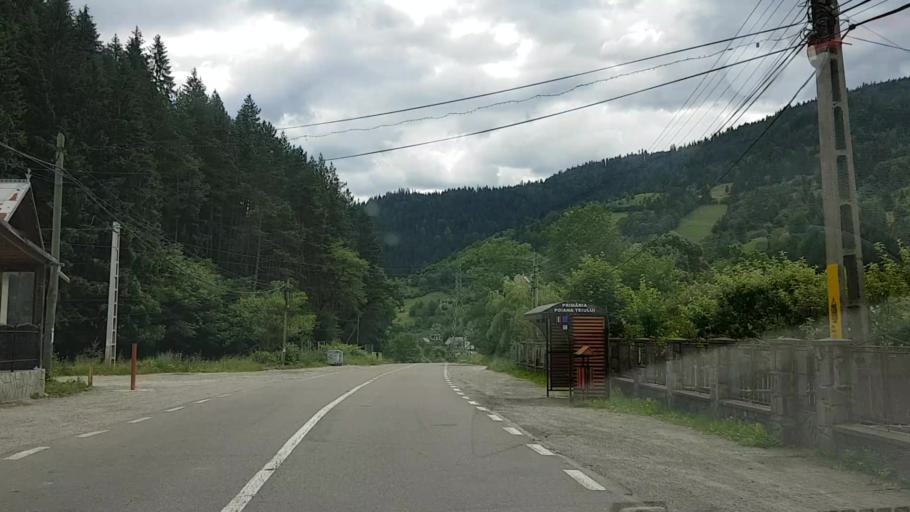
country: RO
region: Neamt
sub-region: Comuna Poiana Teiului
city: Poiana Teiului
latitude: 47.1241
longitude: 25.9071
